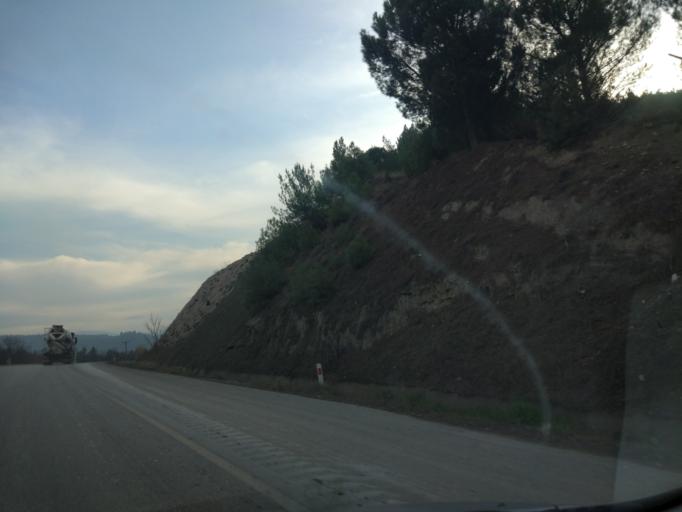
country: TR
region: Karabuk
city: Karabuk
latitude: 41.1651
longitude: 32.6398
